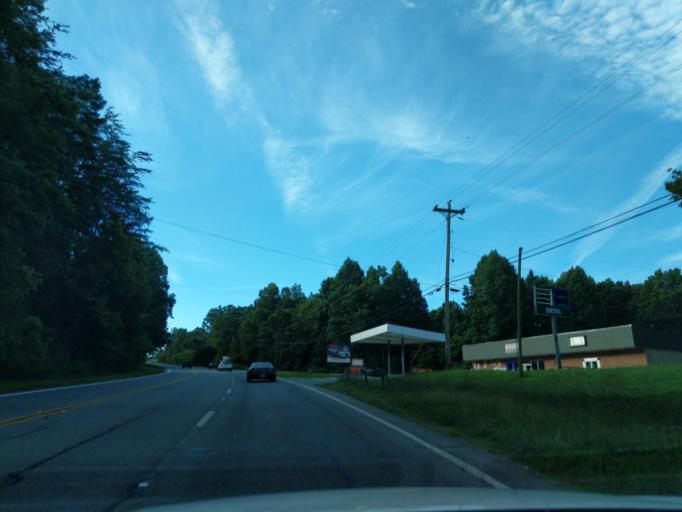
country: US
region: Georgia
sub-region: Fannin County
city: Blue Ridge
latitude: 34.9075
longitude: -84.3768
